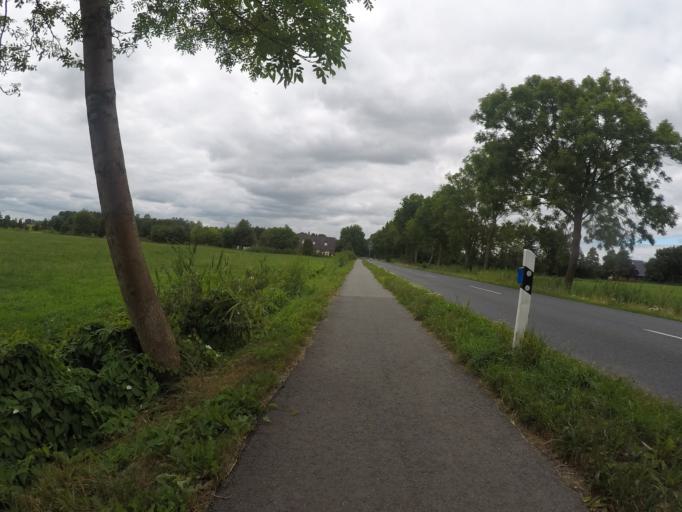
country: DE
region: Lower Saxony
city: Grossenworden
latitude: 53.6744
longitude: 9.2780
